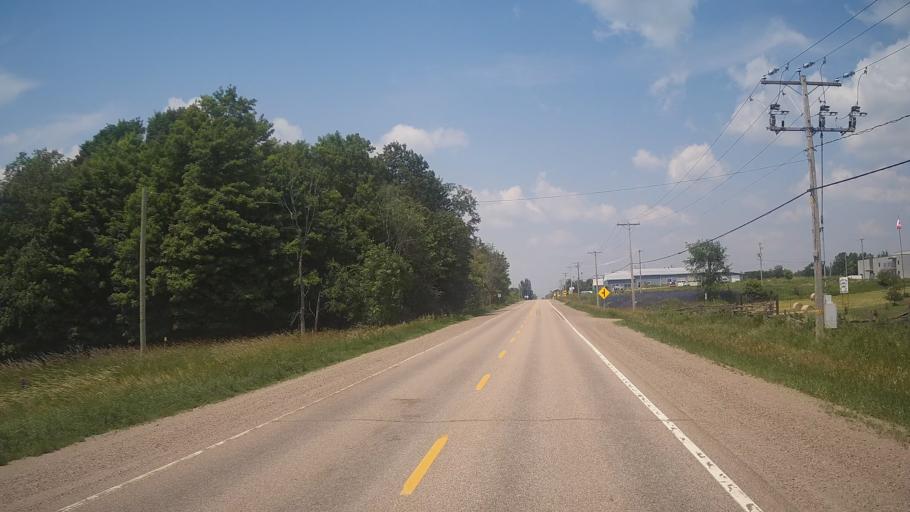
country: CA
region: Quebec
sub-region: Outaouais
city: Shawville
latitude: 45.5953
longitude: -76.4820
